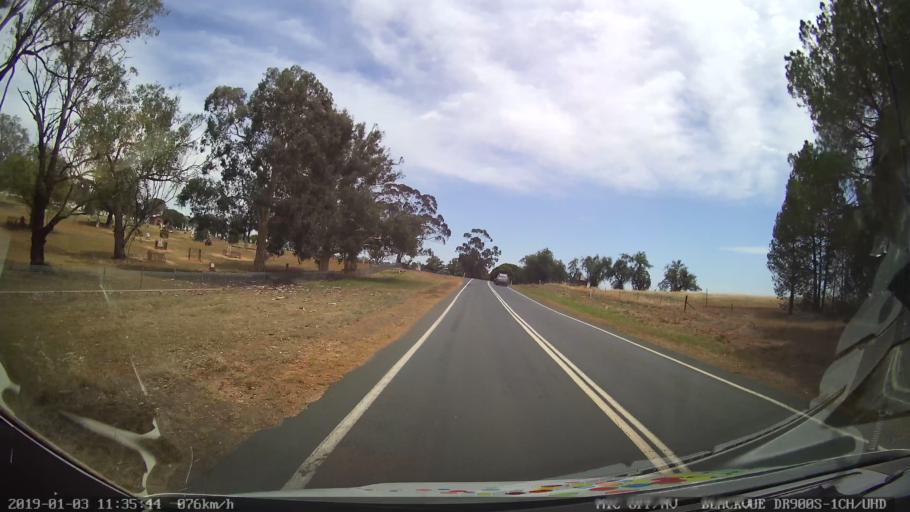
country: AU
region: New South Wales
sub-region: Weddin
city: Grenfell
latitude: -33.9187
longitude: 148.1595
